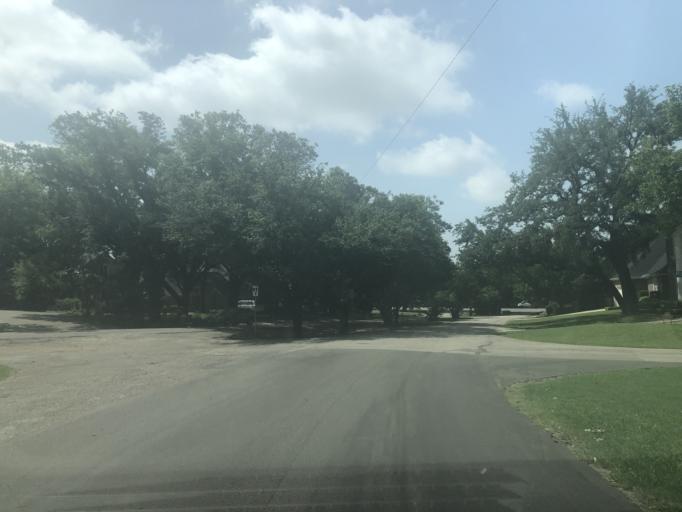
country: US
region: Texas
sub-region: Dallas County
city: University Park
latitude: 32.8649
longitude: -96.8330
